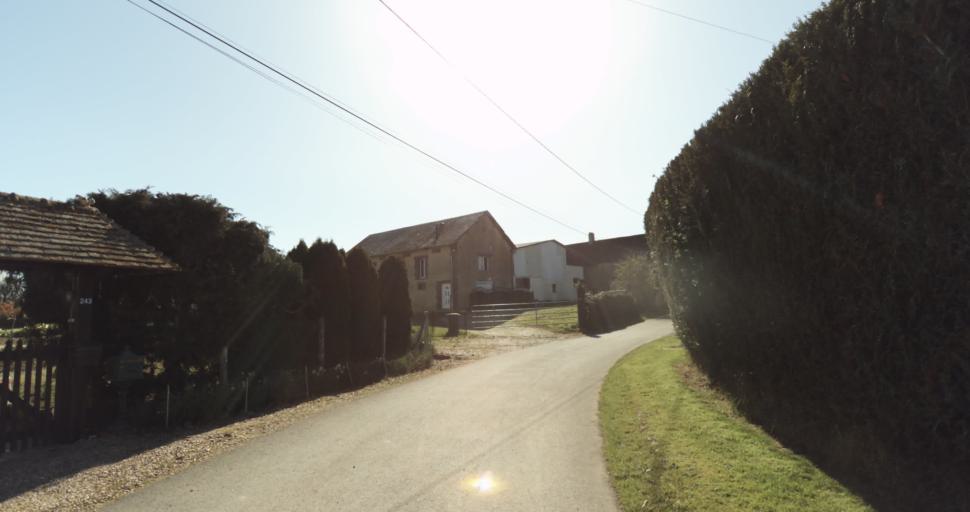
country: FR
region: Lower Normandy
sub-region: Departement du Calvados
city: Saint-Pierre-sur-Dives
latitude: 48.9709
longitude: -0.0026
